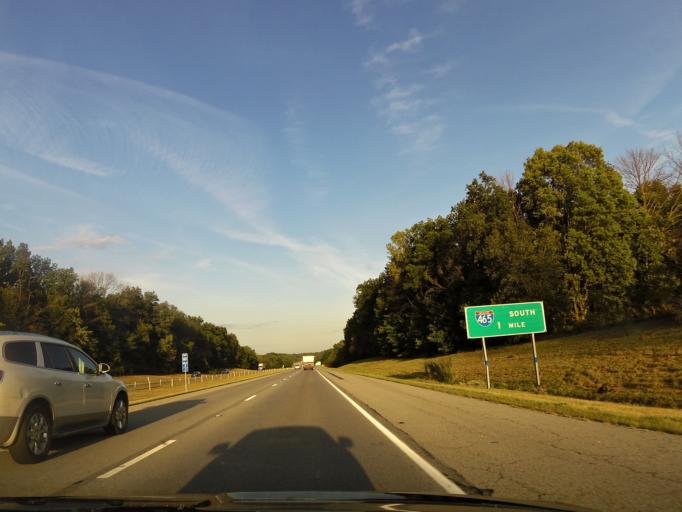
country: US
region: Indiana
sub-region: Boone County
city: Zionsville
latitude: 39.9309
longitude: -86.2940
